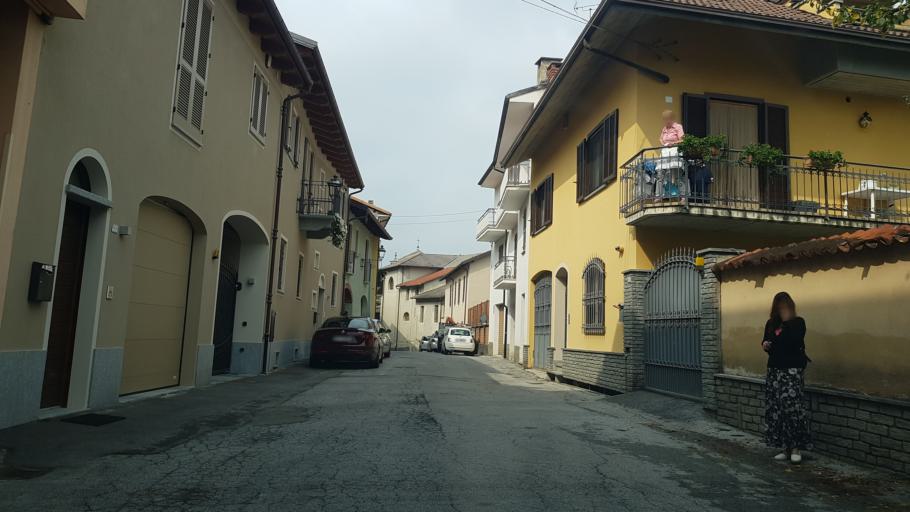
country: IT
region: Piedmont
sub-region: Provincia di Cuneo
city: Peveragno
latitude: 44.3296
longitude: 7.6153
